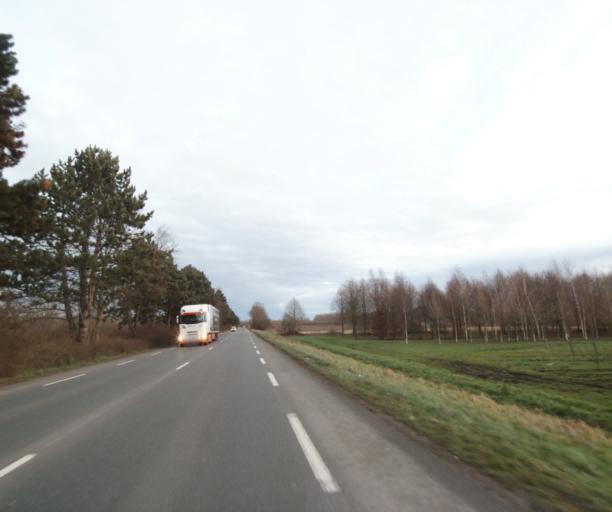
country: FR
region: Nord-Pas-de-Calais
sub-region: Departement du Nord
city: Vicq
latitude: 50.4224
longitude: 3.5956
